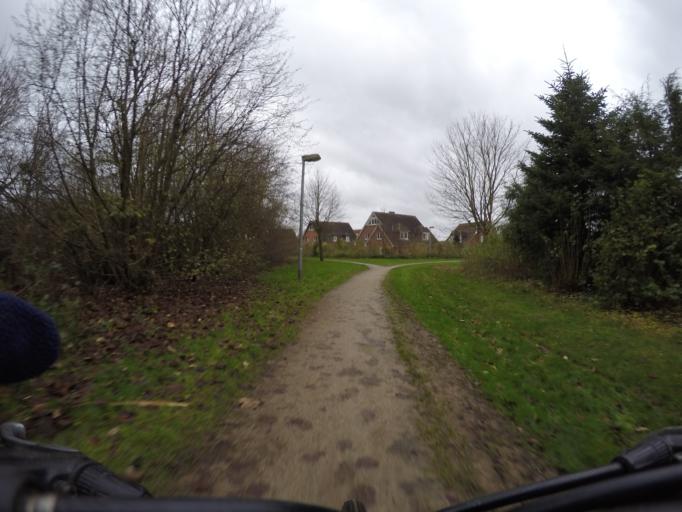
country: DE
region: Schleswig-Holstein
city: Quickborn
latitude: 53.7254
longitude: 9.8964
